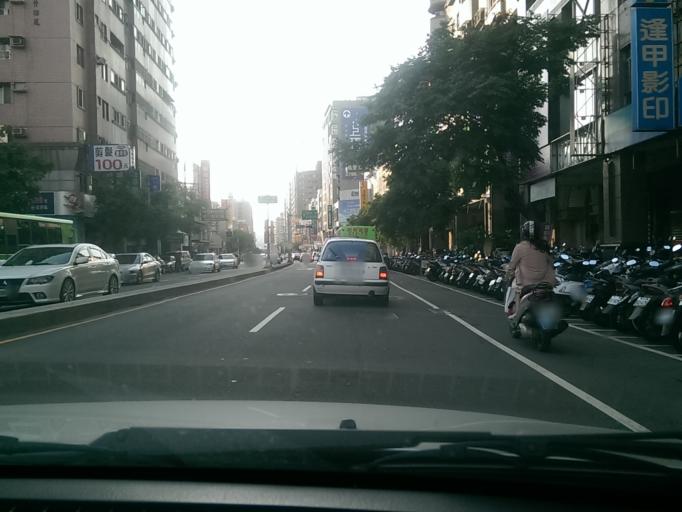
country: TW
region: Taiwan
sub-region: Taichung City
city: Taichung
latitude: 24.1707
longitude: 120.6453
